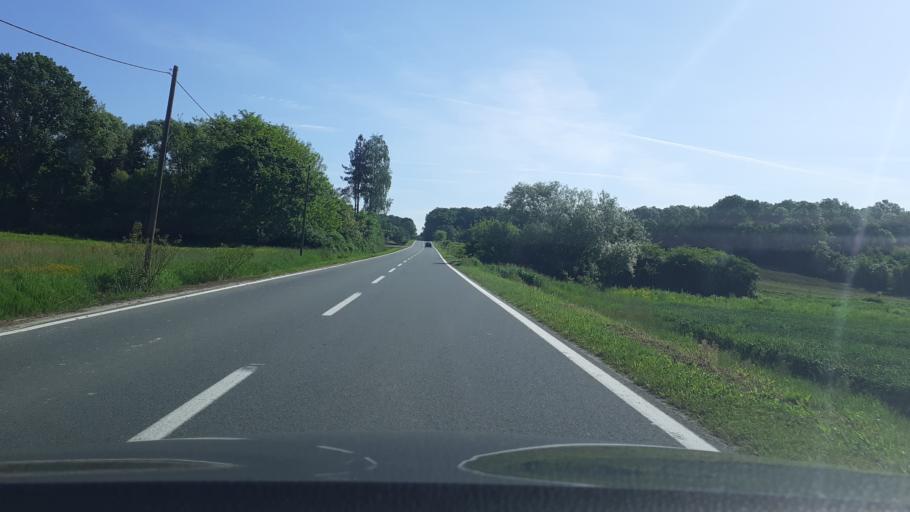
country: HR
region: Brodsko-Posavska
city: Batrina
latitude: 45.2005
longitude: 17.6699
